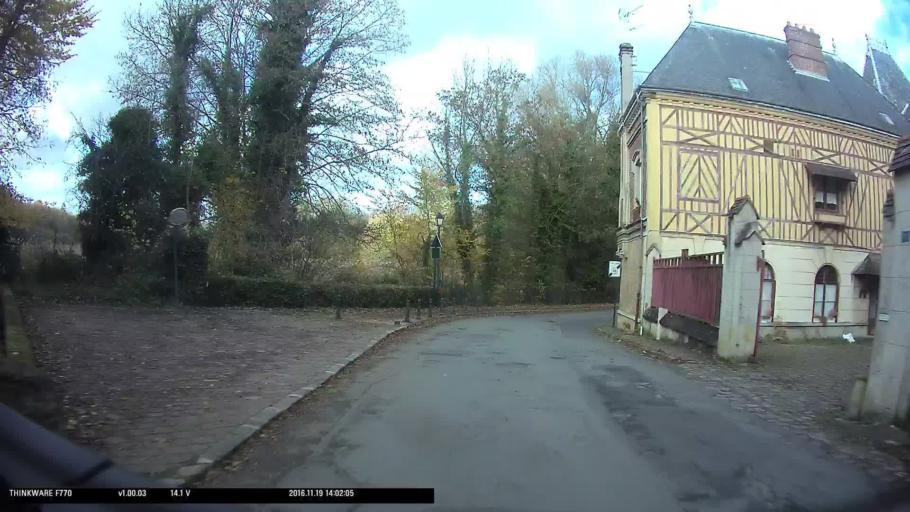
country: FR
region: Ile-de-France
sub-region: Departement du Val-d'Oise
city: Ableiges
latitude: 49.0795
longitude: 2.0027
